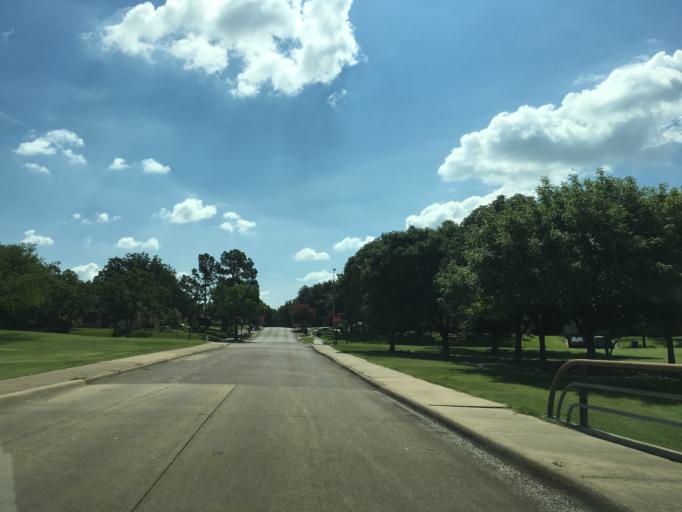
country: US
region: Texas
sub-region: Dallas County
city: Farmers Branch
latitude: 32.9313
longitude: -96.8779
